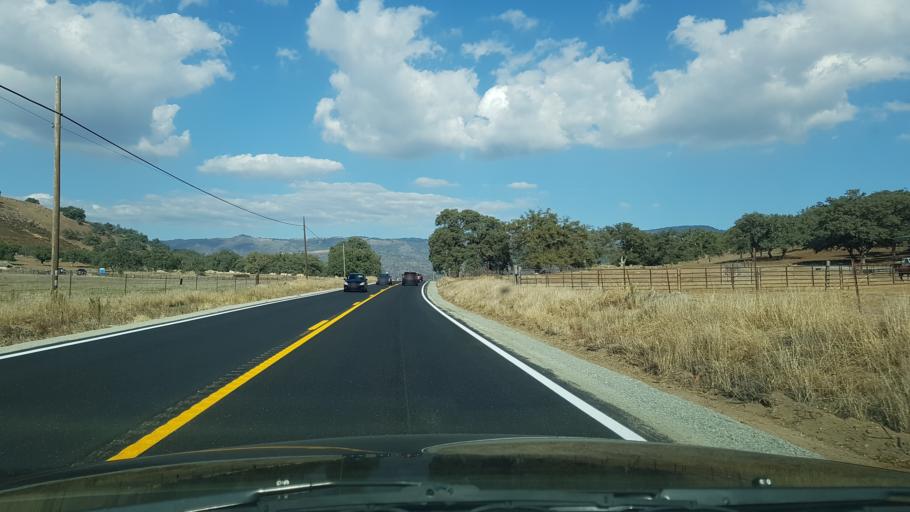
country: US
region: California
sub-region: San Diego County
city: Julian
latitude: 33.1004
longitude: -116.6972
